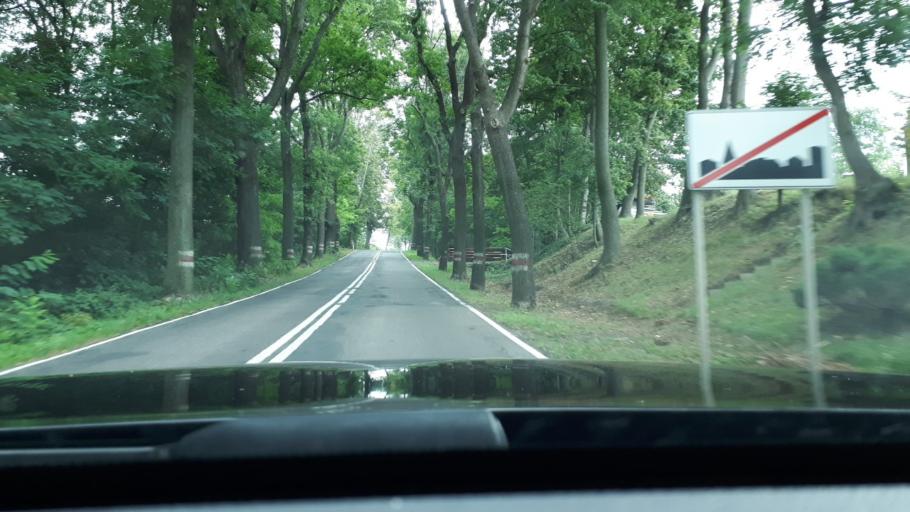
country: PL
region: Lower Silesian Voivodeship
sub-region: Powiat lwowecki
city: Wlen
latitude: 51.1176
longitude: 15.6928
